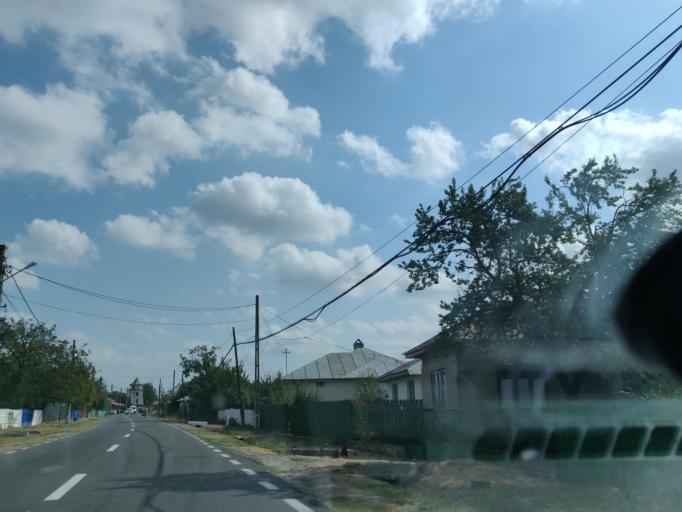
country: RO
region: Vrancea
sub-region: Comuna Ciorasti
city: Ciorasti
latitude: 45.4310
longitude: 27.3085
